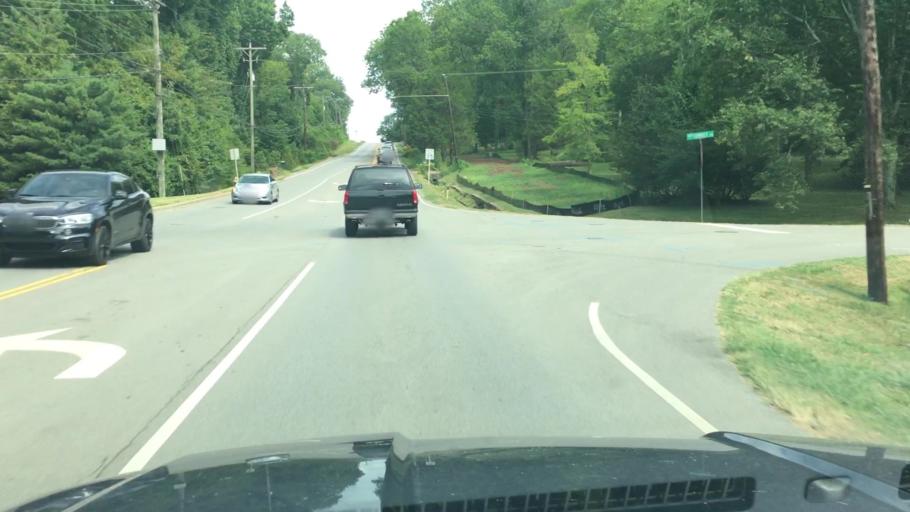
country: US
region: Tennessee
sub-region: Davidson County
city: Oak Hill
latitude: 36.0903
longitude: -86.8129
